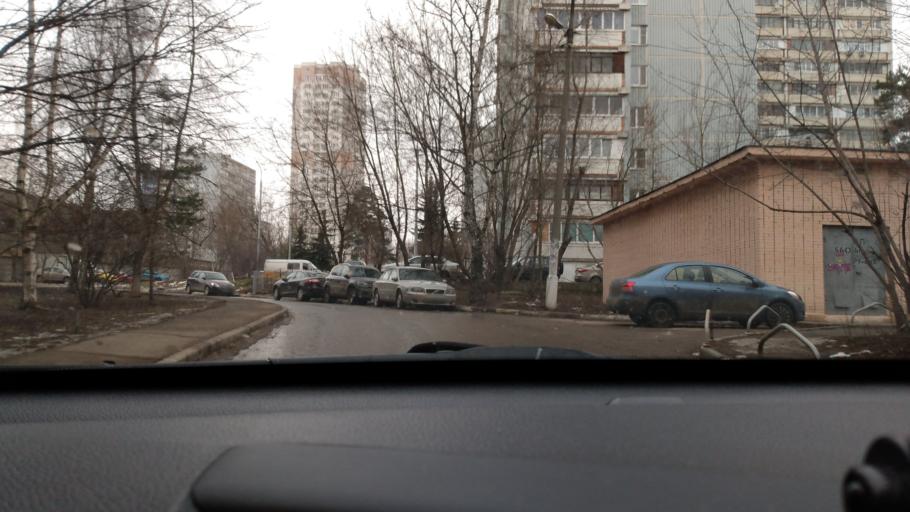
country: RU
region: Moskovskaya
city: Odintsovo
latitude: 55.6650
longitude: 37.2928
